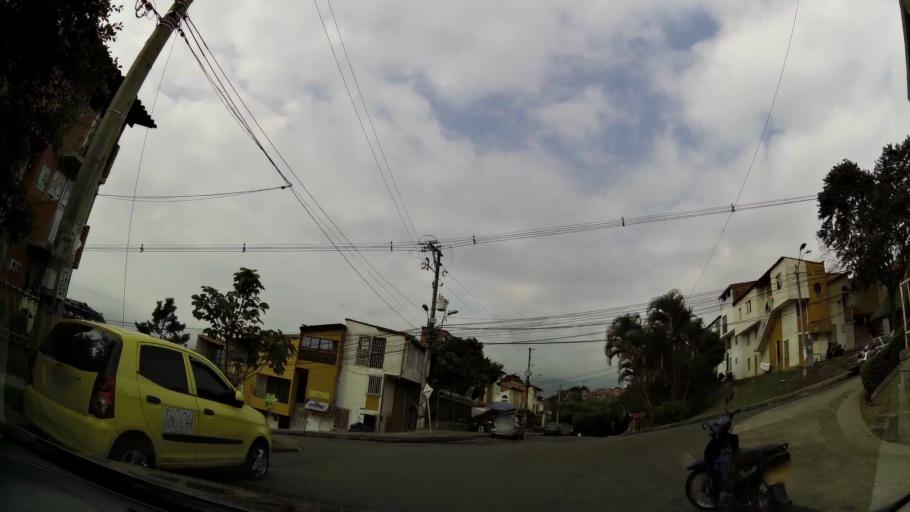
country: CO
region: Antioquia
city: Medellin
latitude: 6.2832
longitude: -75.6013
